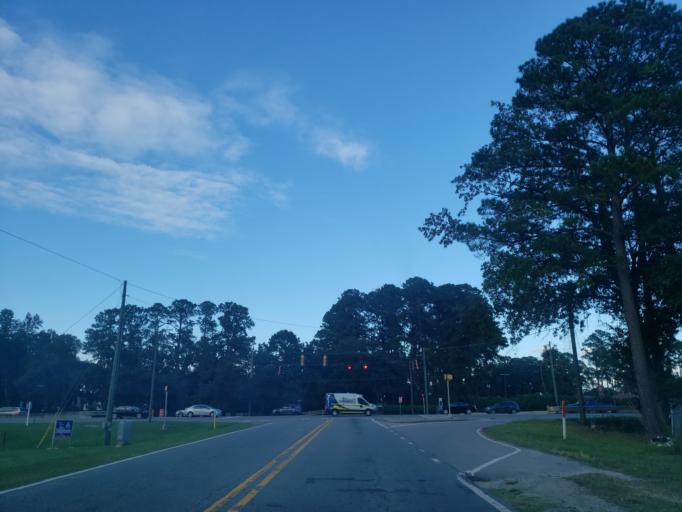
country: US
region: Georgia
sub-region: Chatham County
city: Georgetown
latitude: 31.9903
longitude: -81.2273
